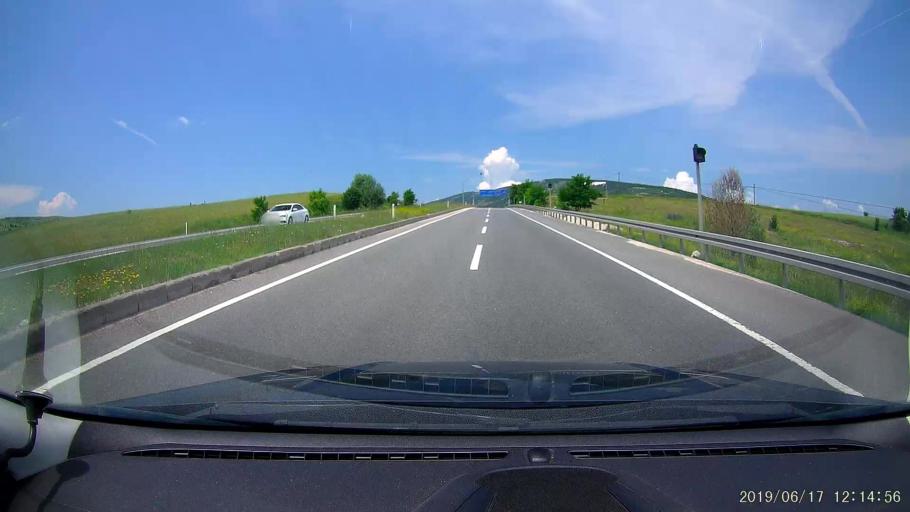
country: TR
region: Karabuk
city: Gozyeri
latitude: 40.8698
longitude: 32.5877
